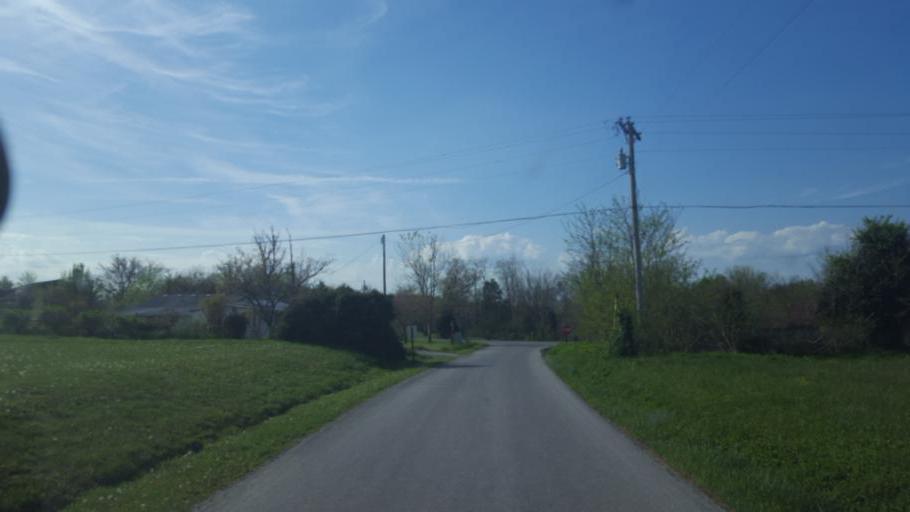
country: US
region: Kentucky
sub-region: Hart County
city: Munfordville
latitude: 37.3193
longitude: -86.0943
